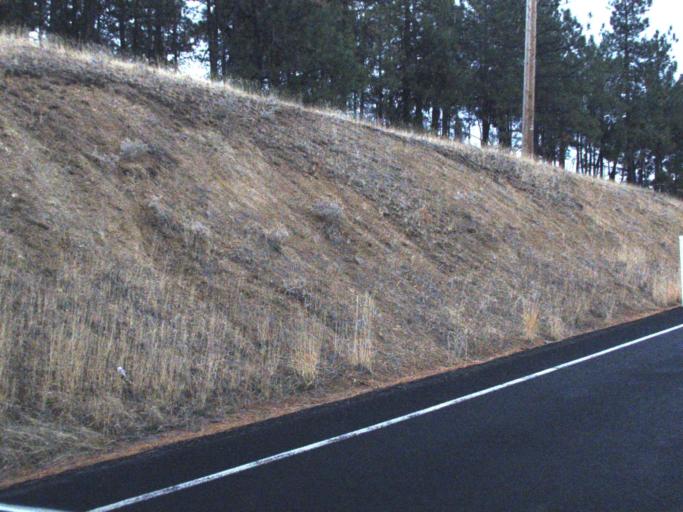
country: US
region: Washington
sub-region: Lincoln County
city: Davenport
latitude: 47.8154
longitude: -118.1825
